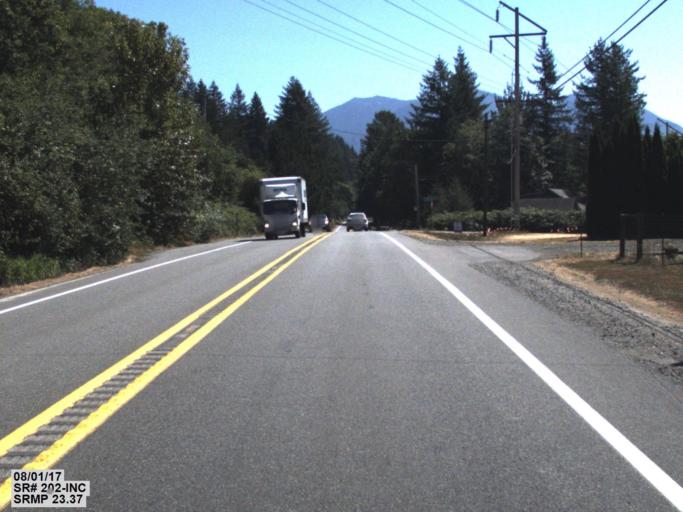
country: US
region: Washington
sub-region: King County
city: Fall City
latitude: 47.5606
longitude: -121.8586
